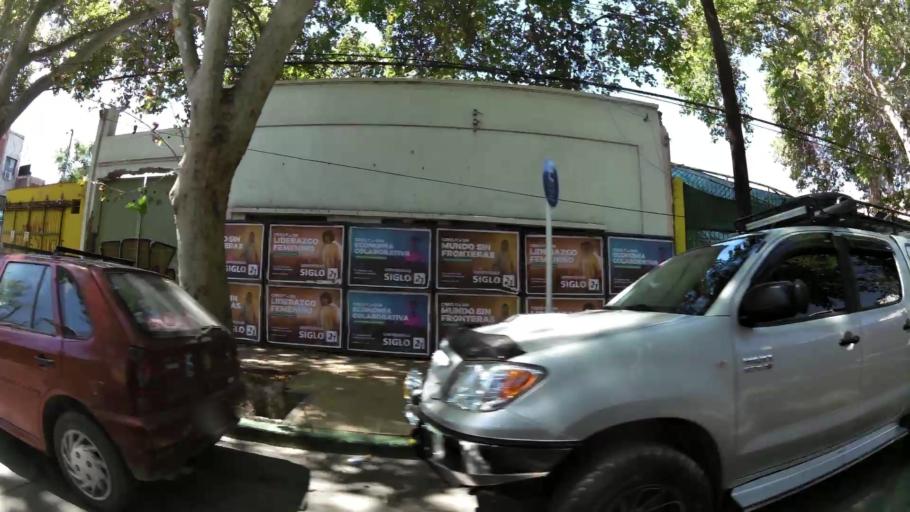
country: AR
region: Mendoza
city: Mendoza
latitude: -32.8893
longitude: -68.8315
